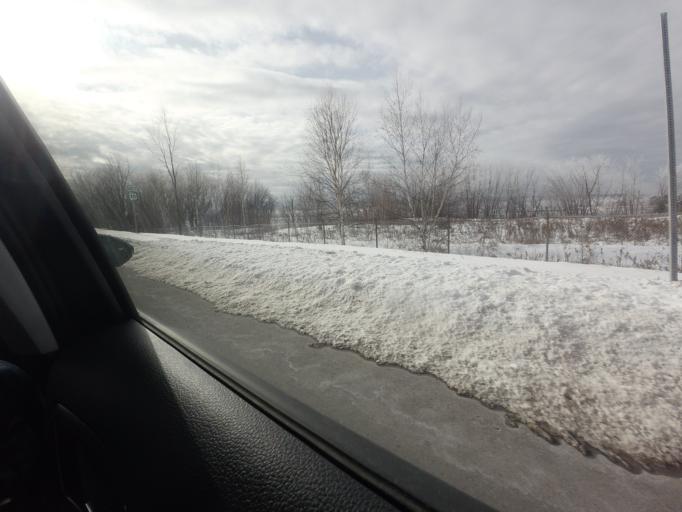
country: CA
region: New Brunswick
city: Fredericton
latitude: 45.9570
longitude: -66.6234
